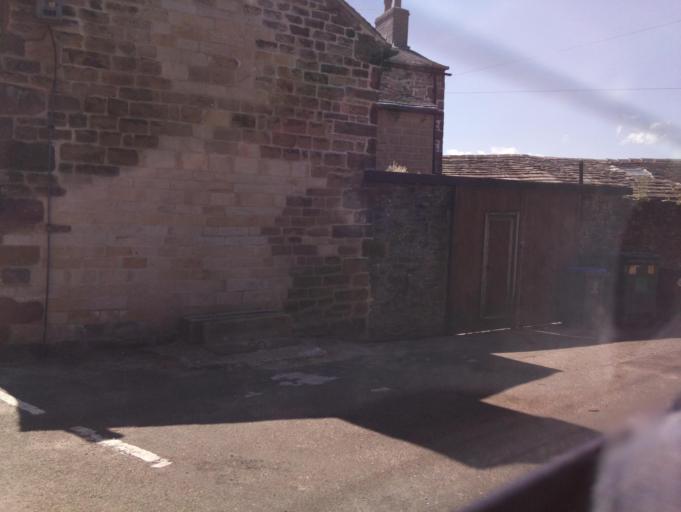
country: GB
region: England
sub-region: Derbyshire
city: Buxton
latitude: 53.1816
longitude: -1.8693
